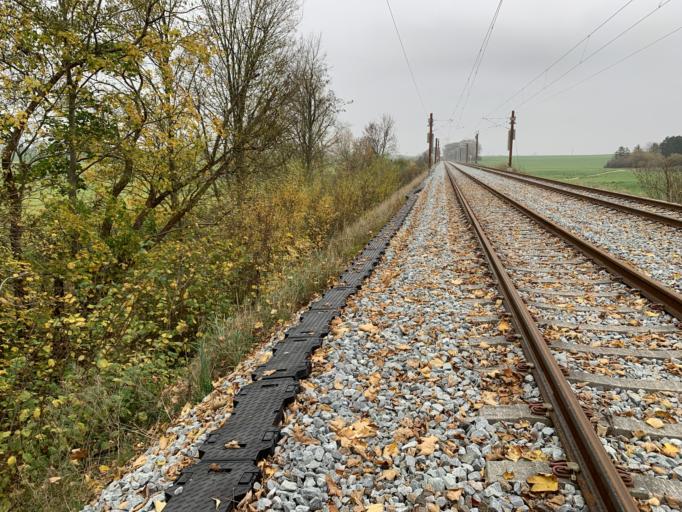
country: DK
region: Zealand
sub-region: Ringsted Kommune
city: Ringsted
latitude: 55.4150
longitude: 11.7515
